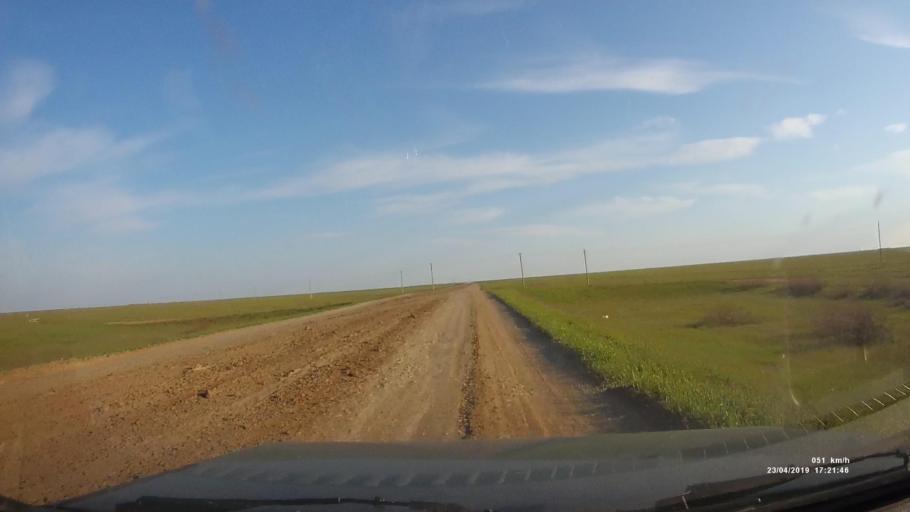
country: RU
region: Kalmykiya
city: Priyutnoye
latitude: 46.1735
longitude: 43.5058
